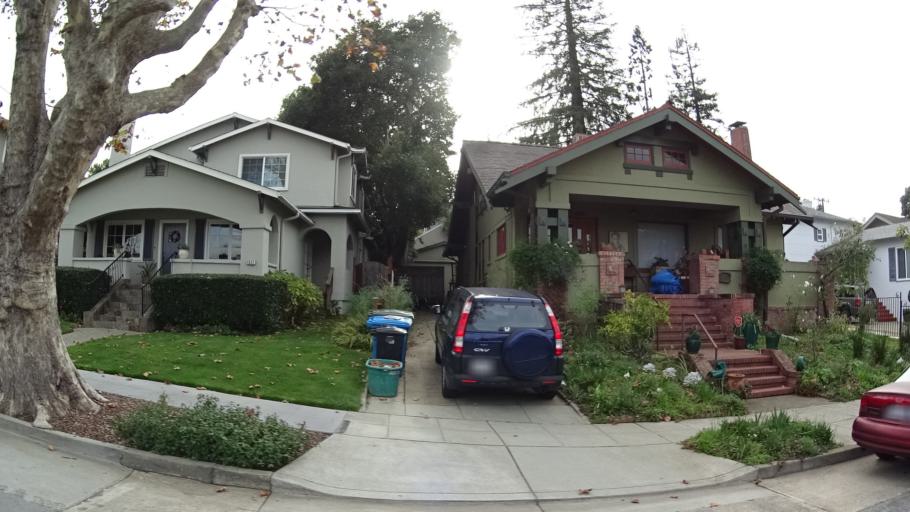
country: US
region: California
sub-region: San Mateo County
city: Hillsborough
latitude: 37.5802
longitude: -122.3772
